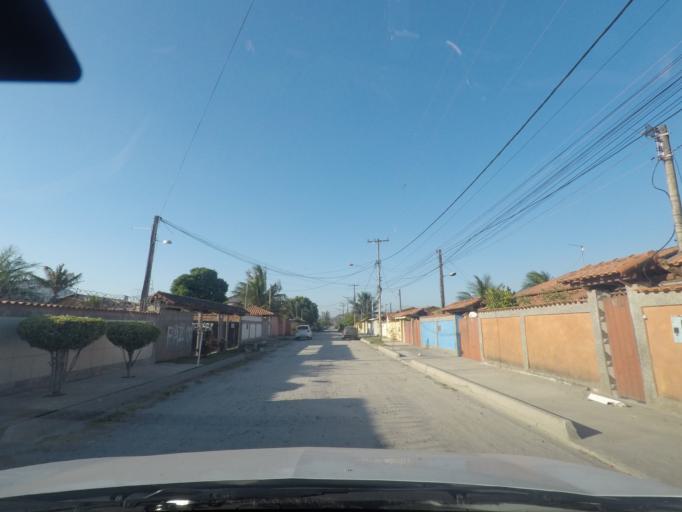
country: BR
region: Rio de Janeiro
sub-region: Marica
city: Marica
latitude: -22.9657
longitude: -42.9370
